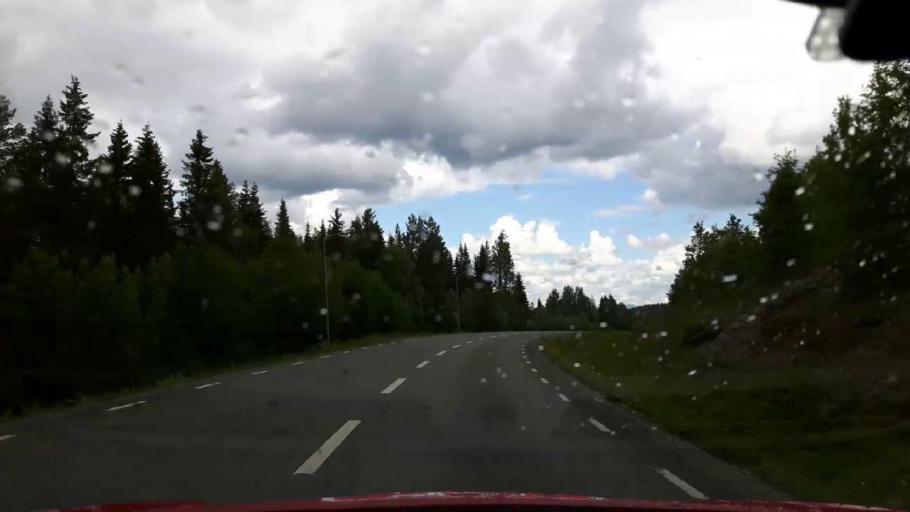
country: SE
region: Jaemtland
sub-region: Krokoms Kommun
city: Krokom
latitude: 63.7605
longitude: 14.3135
